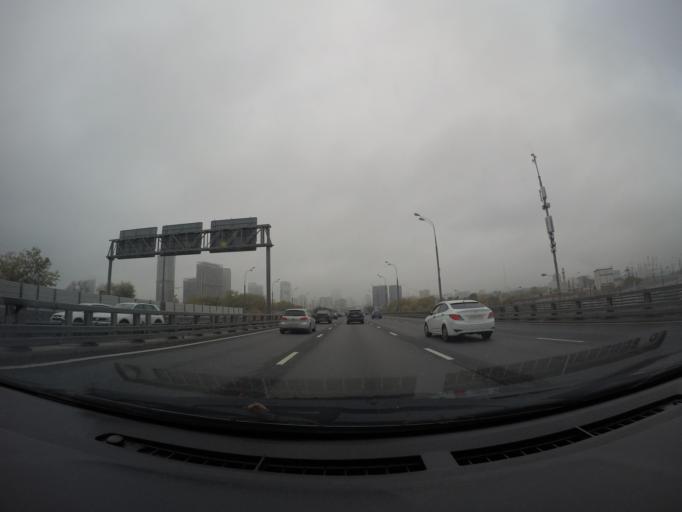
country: RU
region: Moscow
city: Sokol
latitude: 55.7695
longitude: 37.5125
